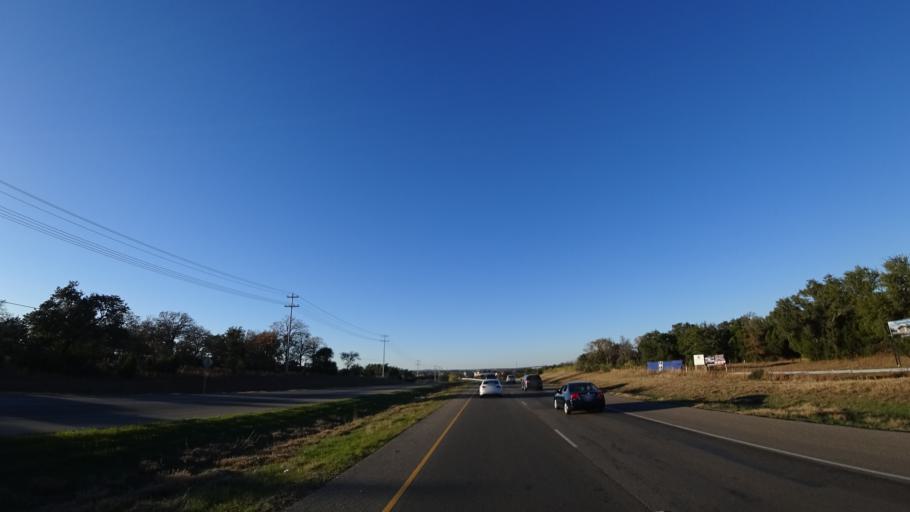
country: US
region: Texas
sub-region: Williamson County
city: Brushy Creek
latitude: 30.5254
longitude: -97.7757
